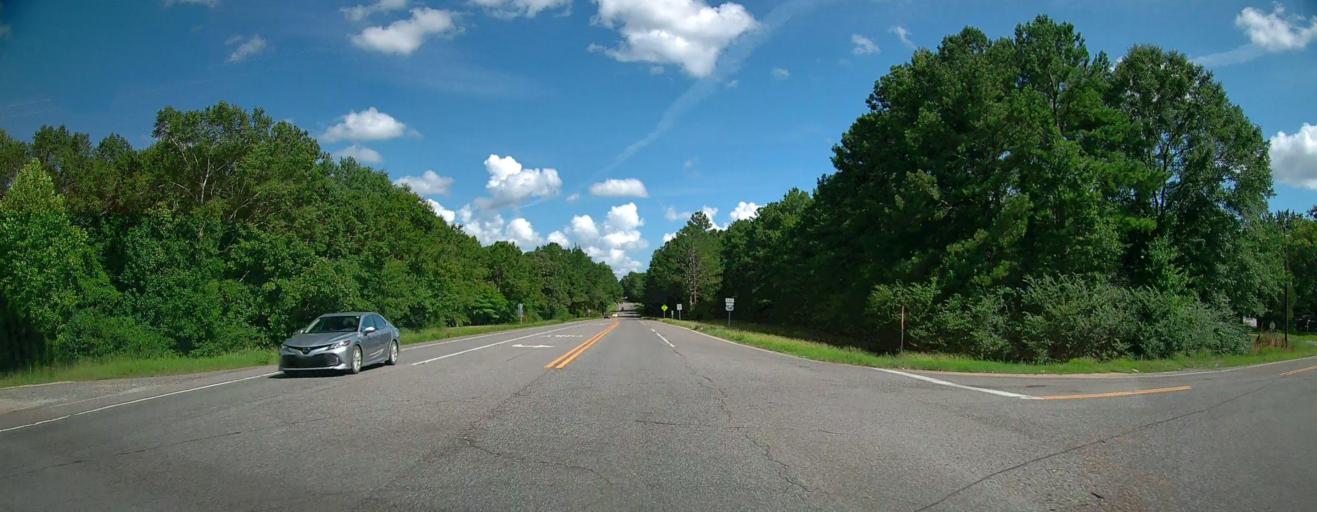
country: US
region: Alabama
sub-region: Pickens County
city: Gordo
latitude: 33.2965
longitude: -87.8767
